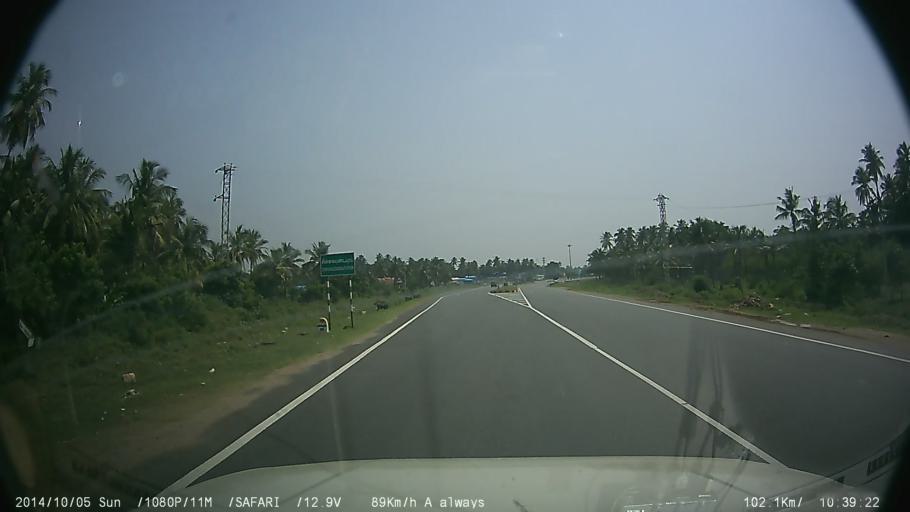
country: IN
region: Tamil Nadu
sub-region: Salem
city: Salem
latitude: 11.6656
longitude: 78.2521
